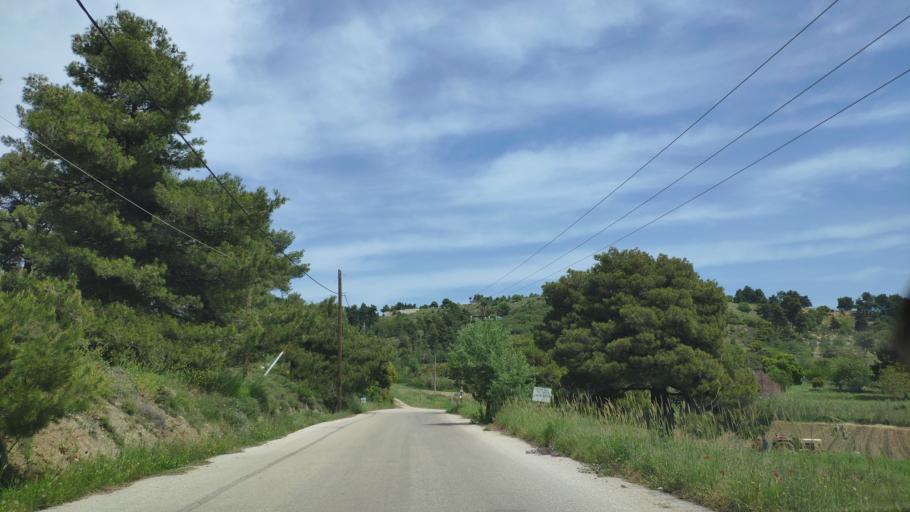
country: GR
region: Attica
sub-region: Nomarchia Anatolikis Attikis
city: Varnavas
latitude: 38.2276
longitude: 23.9303
